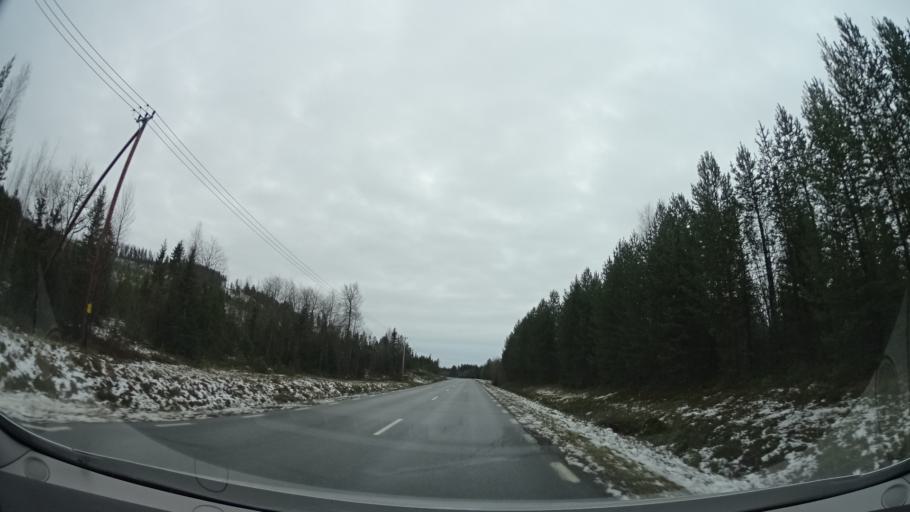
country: SE
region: Jaemtland
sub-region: Stroemsunds Kommun
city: Stroemsund
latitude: 63.9630
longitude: 15.4830
